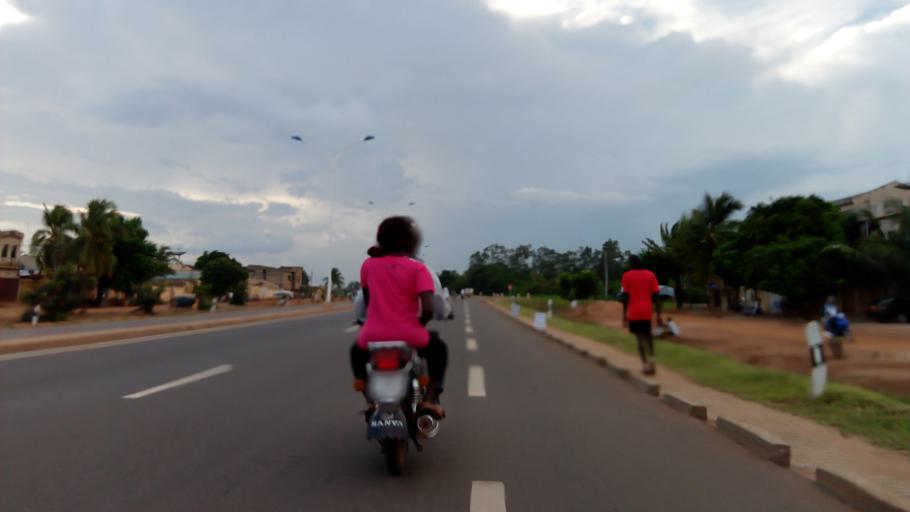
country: TG
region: Maritime
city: Lome
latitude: 6.2441
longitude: 1.1930
